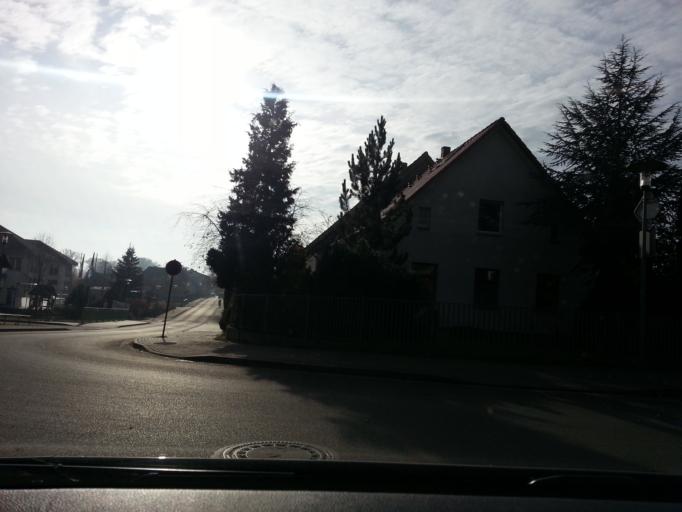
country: DE
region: Mecklenburg-Vorpommern
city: Torgelow
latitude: 53.6327
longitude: 14.0170
